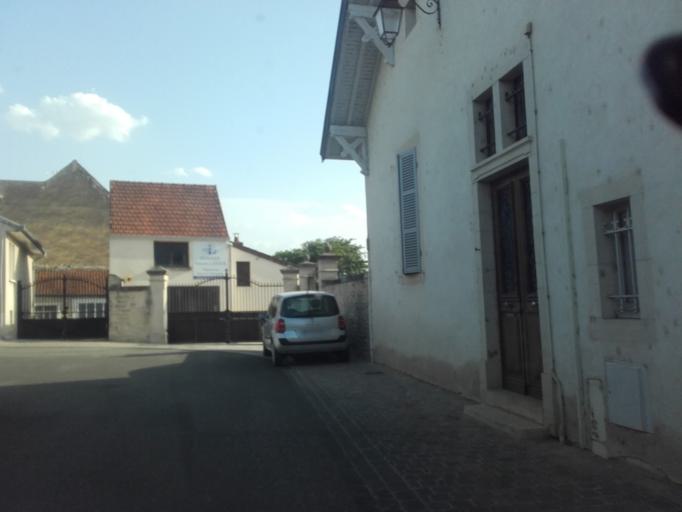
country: FR
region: Bourgogne
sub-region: Departement de la Cote-d'Or
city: Meursault
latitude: 46.9791
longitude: 4.7684
